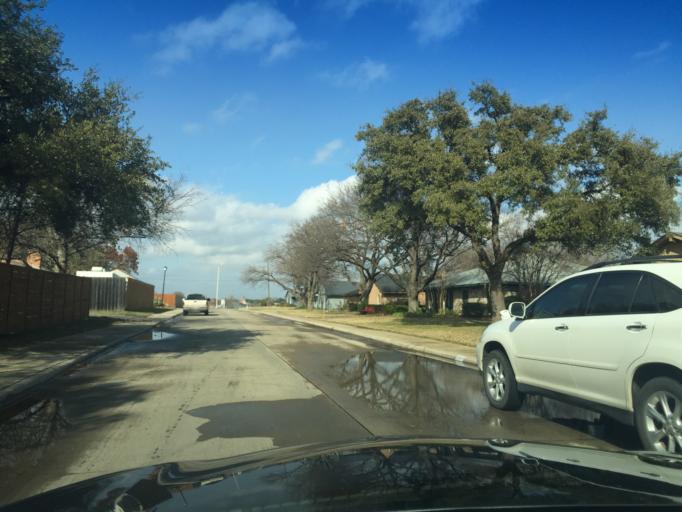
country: US
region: Texas
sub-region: Dallas County
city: Carrollton
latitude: 32.9830
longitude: -96.8933
